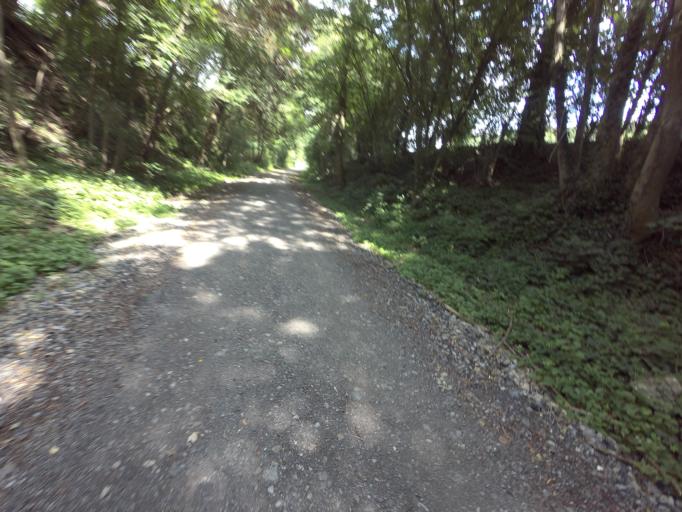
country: BE
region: Wallonia
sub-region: Province de Liege
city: Plombieres
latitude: 50.7134
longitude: 5.9778
